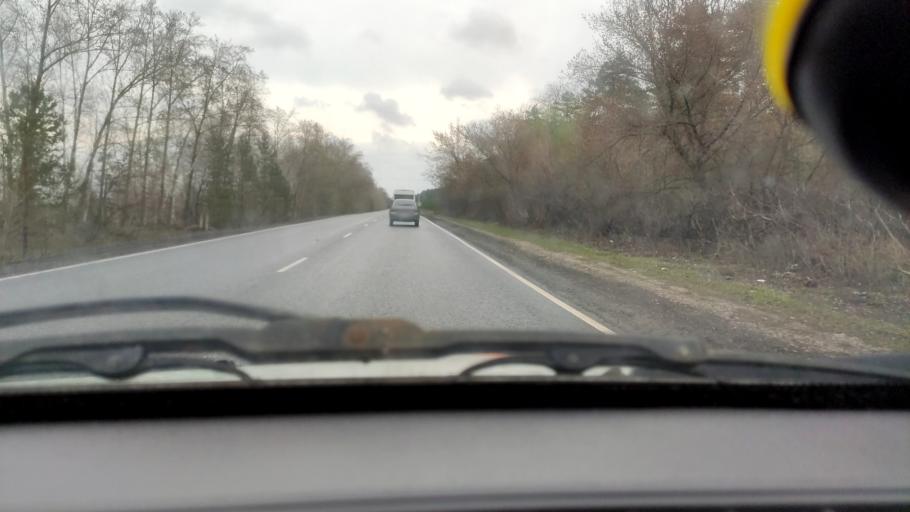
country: RU
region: Samara
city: Povolzhskiy
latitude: 53.6210
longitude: 49.6411
